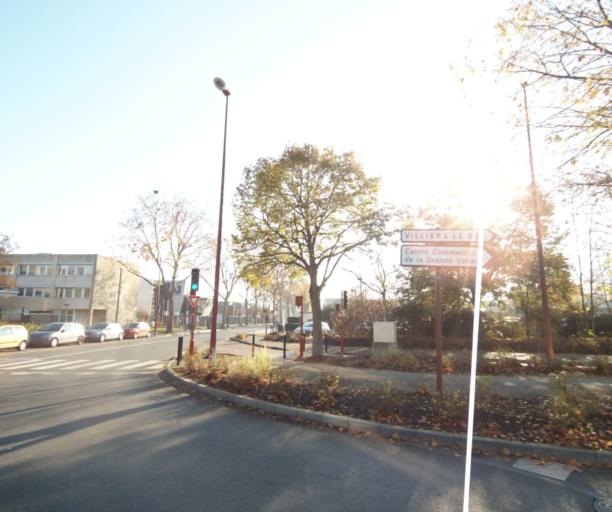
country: FR
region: Ile-de-France
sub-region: Departement du Val-d'Oise
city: Gonesse
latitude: 48.9919
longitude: 2.4323
